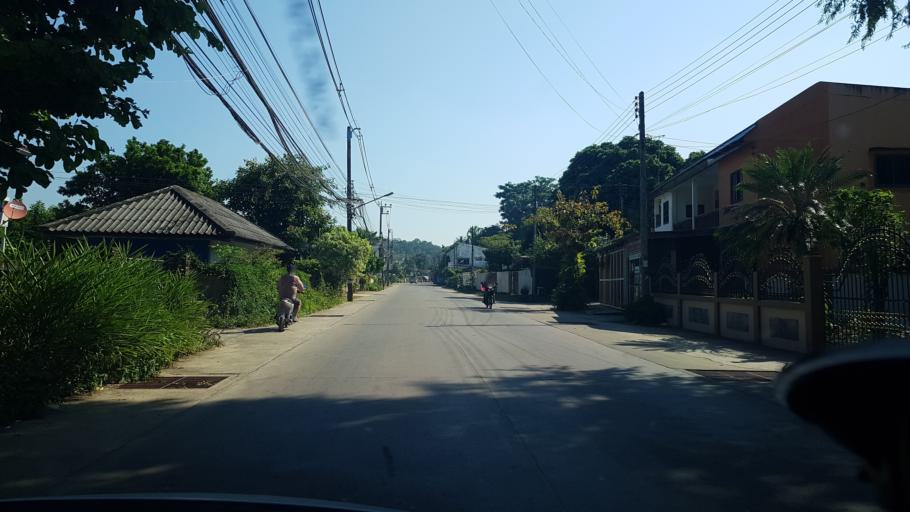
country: TH
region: Chiang Rai
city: Chiang Rai
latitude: 19.9079
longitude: 99.7943
